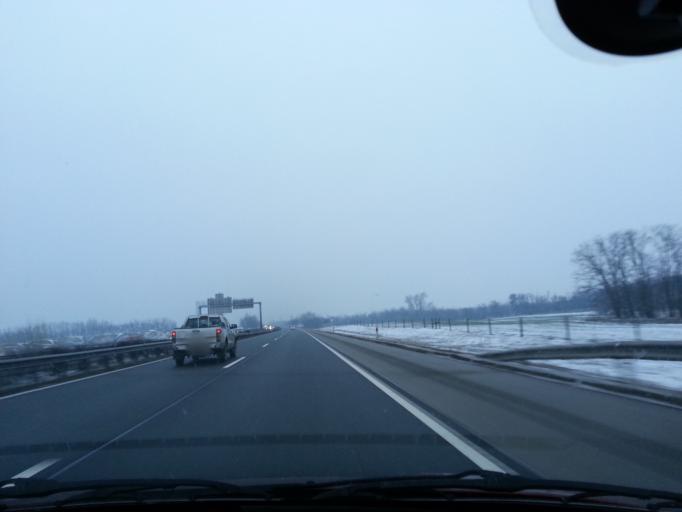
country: HU
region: Pest
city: Felsopakony
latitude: 47.3391
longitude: 19.2180
